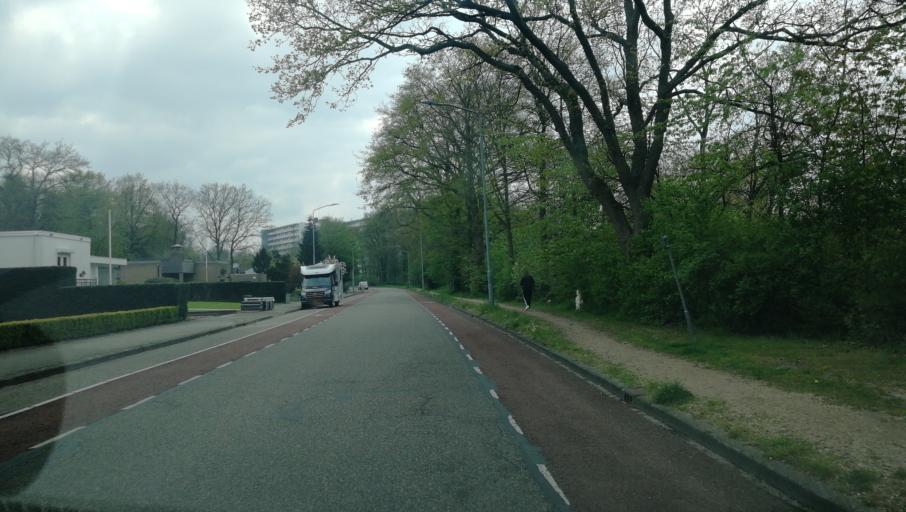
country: NL
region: Limburg
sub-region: Gemeente Venlo
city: Venlo
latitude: 51.3629
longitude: 6.1918
